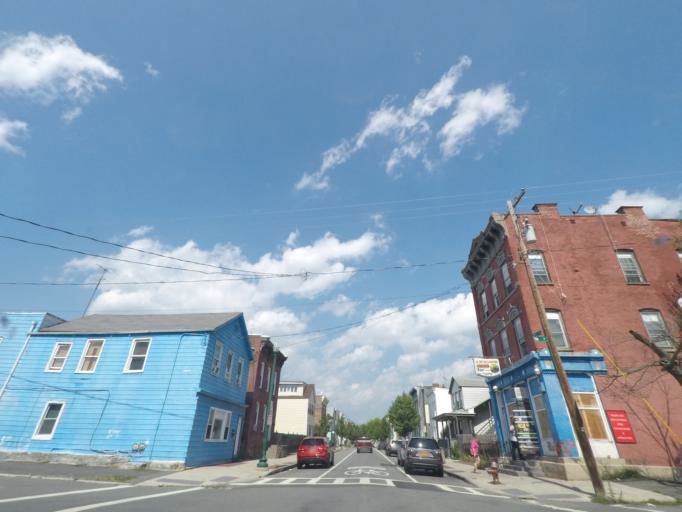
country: US
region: New York
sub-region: Rensselaer County
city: Troy
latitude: 42.7112
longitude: -73.6965
